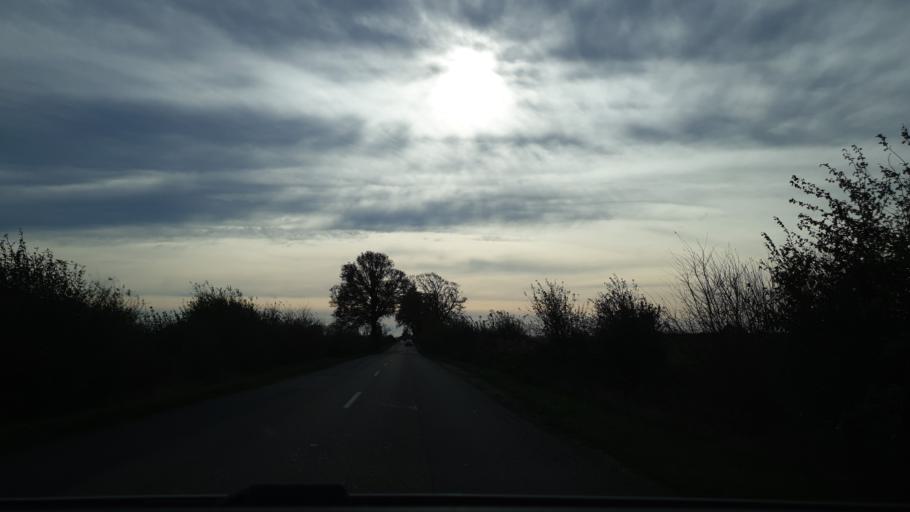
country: PL
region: Pomeranian Voivodeship
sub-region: Powiat pucki
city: Puck
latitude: 54.6918
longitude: 18.3660
